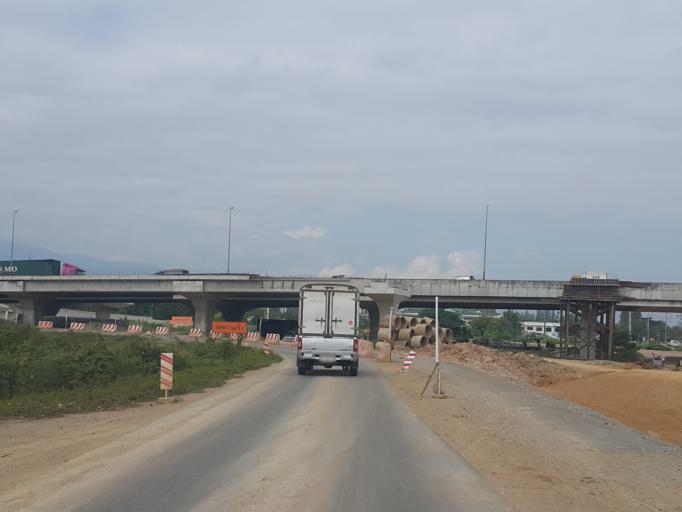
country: TH
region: Chiang Mai
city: Saraphi
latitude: 18.7344
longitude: 99.0374
